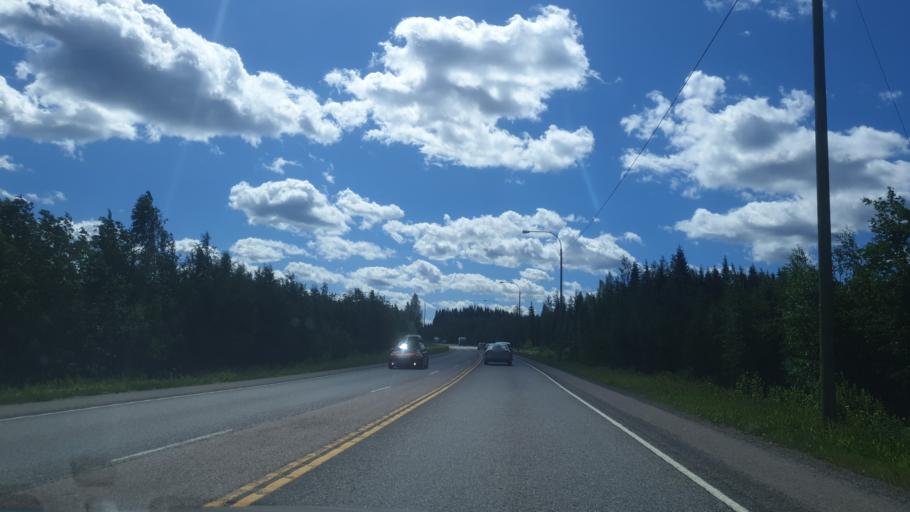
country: FI
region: Northern Savo
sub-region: Varkaus
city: Varkaus
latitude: 62.3859
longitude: 27.8099
